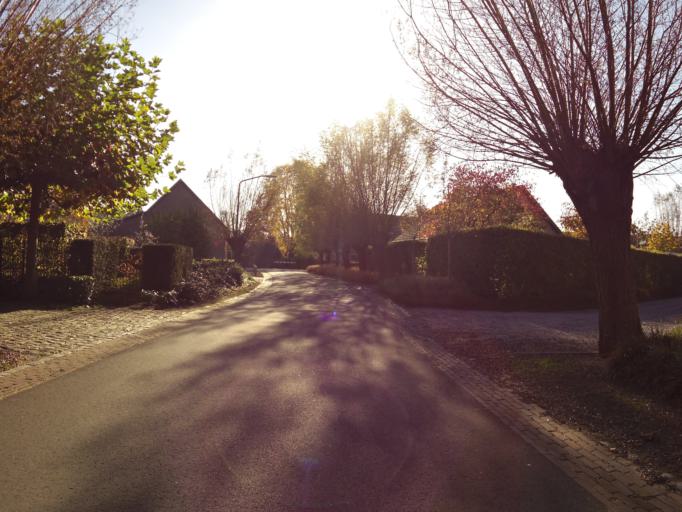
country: NL
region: North Brabant
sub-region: Gemeente Vught
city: Vught
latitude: 51.6155
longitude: 5.2964
